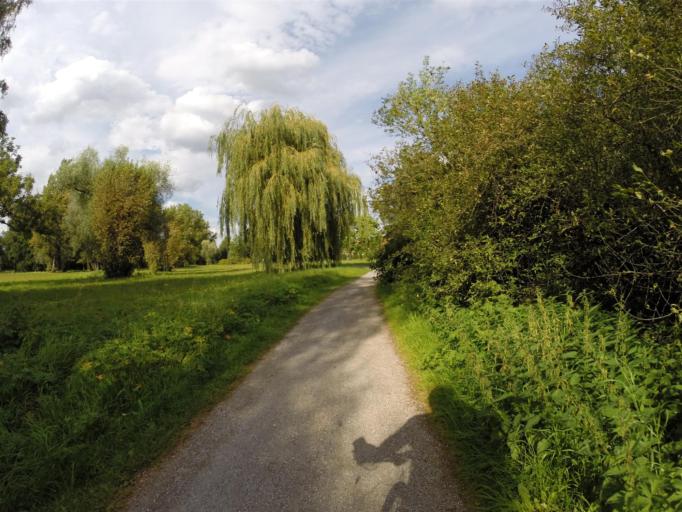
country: DE
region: Thuringia
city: Jena
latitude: 50.9209
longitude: 11.5869
